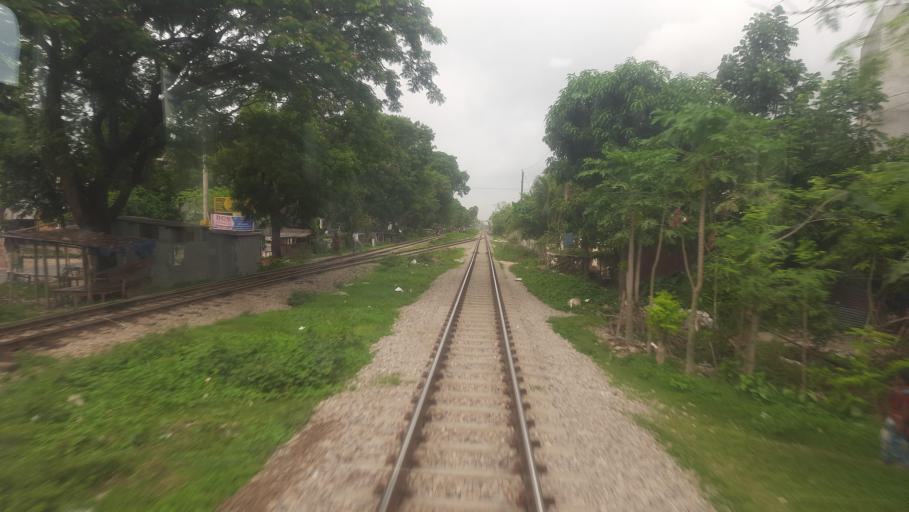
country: BD
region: Dhaka
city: Narsingdi
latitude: 23.9314
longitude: 90.7281
